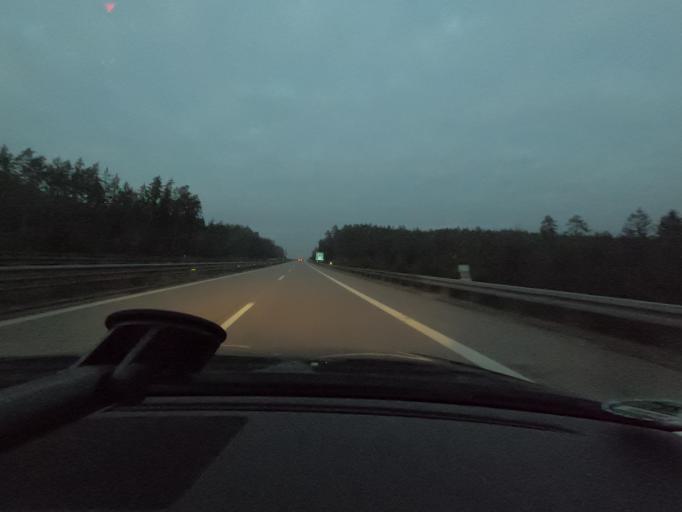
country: DE
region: Bavaria
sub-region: Upper Franconia
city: Niederfullbach
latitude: 50.2093
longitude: 11.0457
